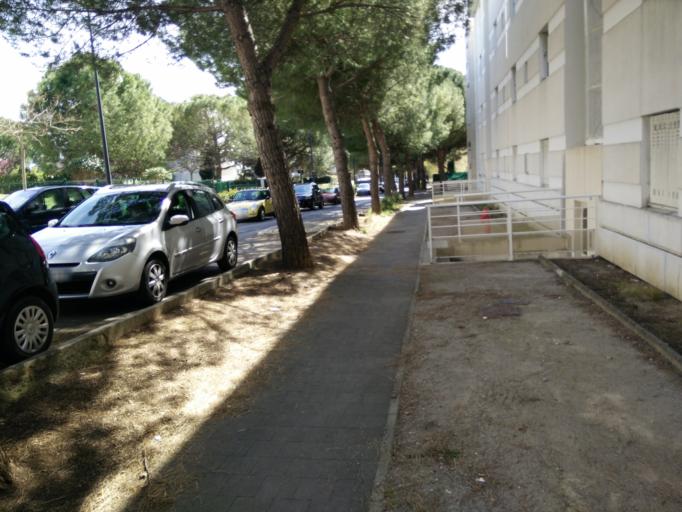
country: FR
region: Languedoc-Roussillon
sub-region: Departement de l'Herault
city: Castelnau-le-Lez
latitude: 43.6160
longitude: 3.9129
